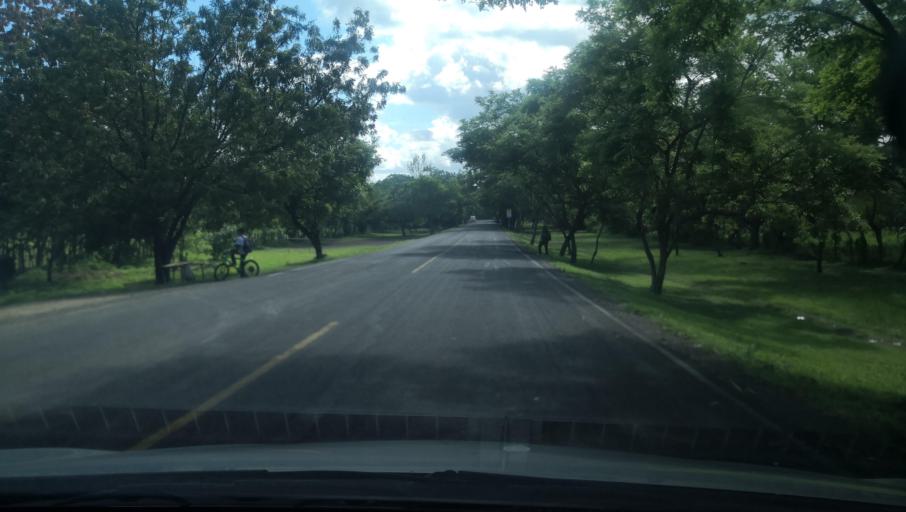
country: NI
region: Madriz
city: Somoto
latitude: 13.4691
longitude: -86.6275
